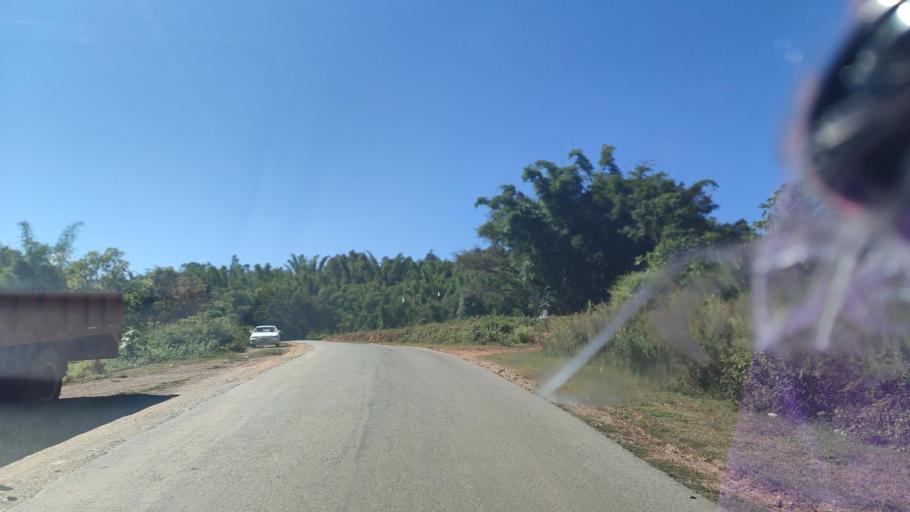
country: MM
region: Shan
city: Taunggyi
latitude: 20.8864
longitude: 97.5450
